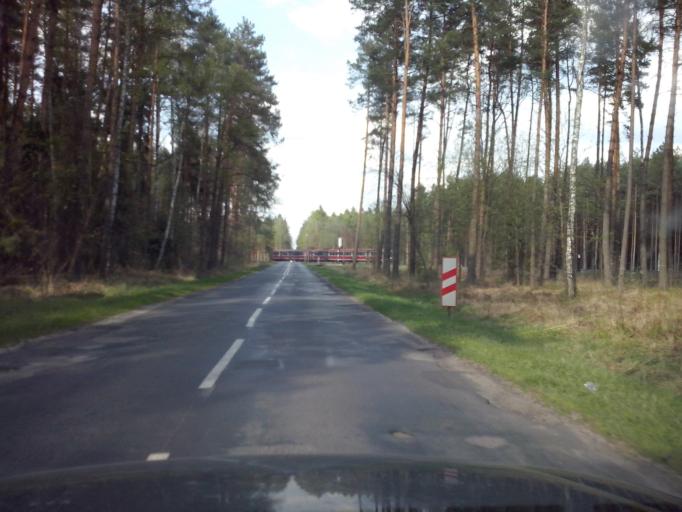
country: PL
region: Subcarpathian Voivodeship
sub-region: Powiat lezajski
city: Letownia
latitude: 50.3714
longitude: 22.2508
